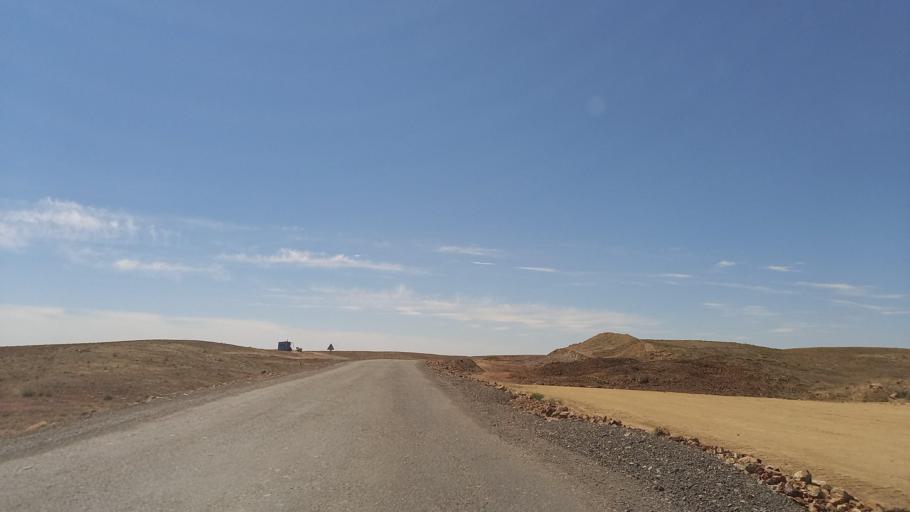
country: KZ
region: Almaty Oblysy
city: Ulken
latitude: 45.0602
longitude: 74.0024
